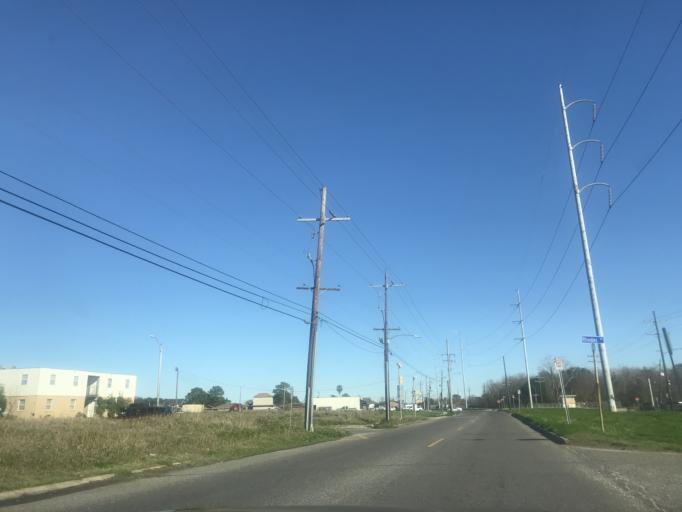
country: US
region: Louisiana
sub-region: Saint Bernard Parish
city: Arabi
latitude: 30.0218
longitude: -90.0013
